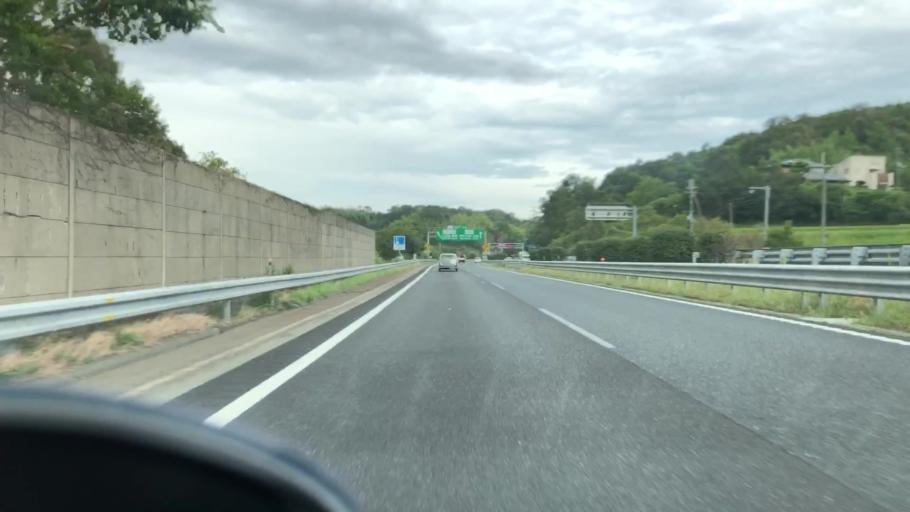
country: JP
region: Hyogo
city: Sandacho
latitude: 34.8903
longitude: 135.1373
